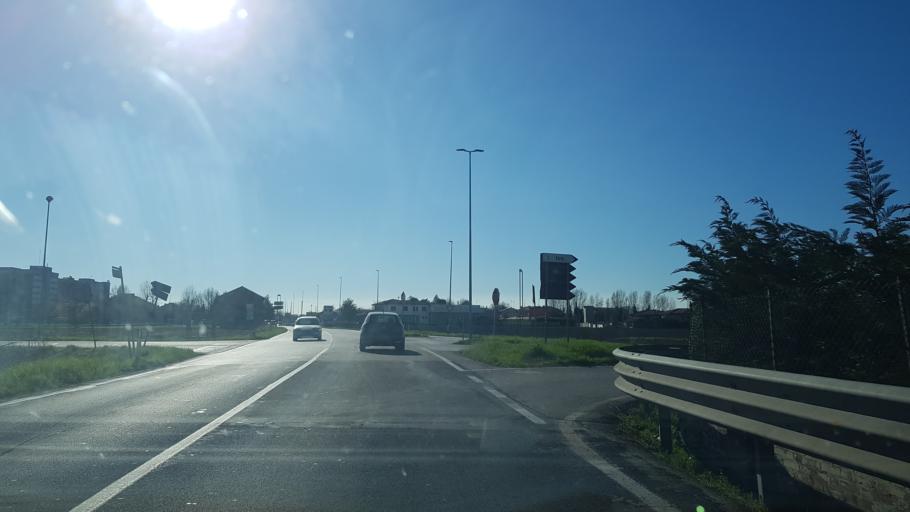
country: IT
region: Veneto
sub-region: Provincia di Rovigo
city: Buso
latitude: 45.0757
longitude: 11.8225
